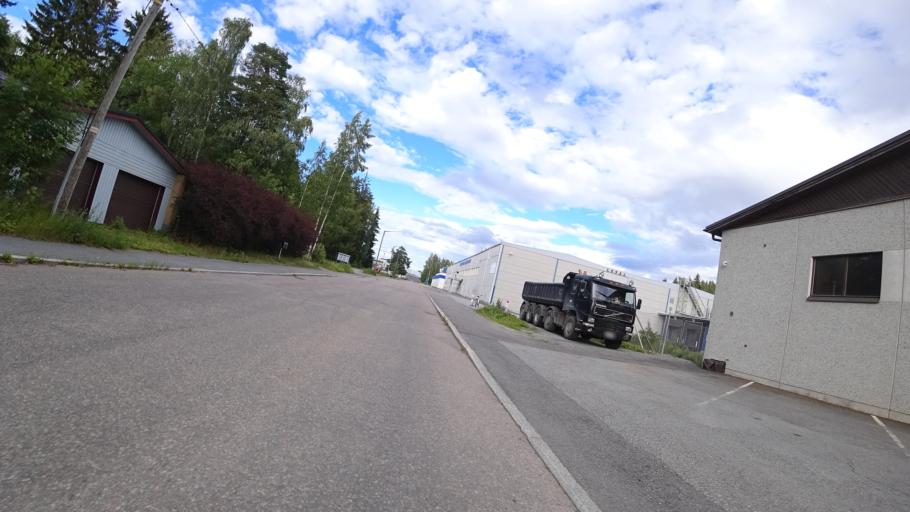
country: FI
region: Pirkanmaa
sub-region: Tampere
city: Pirkkala
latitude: 61.5014
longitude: 23.6171
